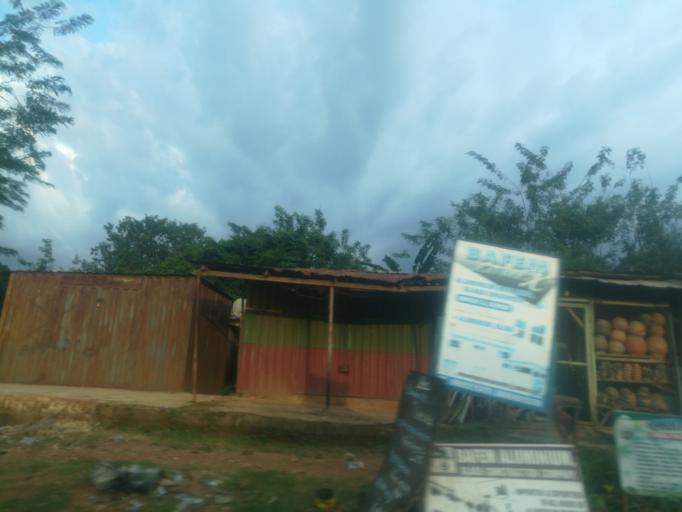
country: NG
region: Oyo
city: Ibadan
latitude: 7.3853
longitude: 3.8363
